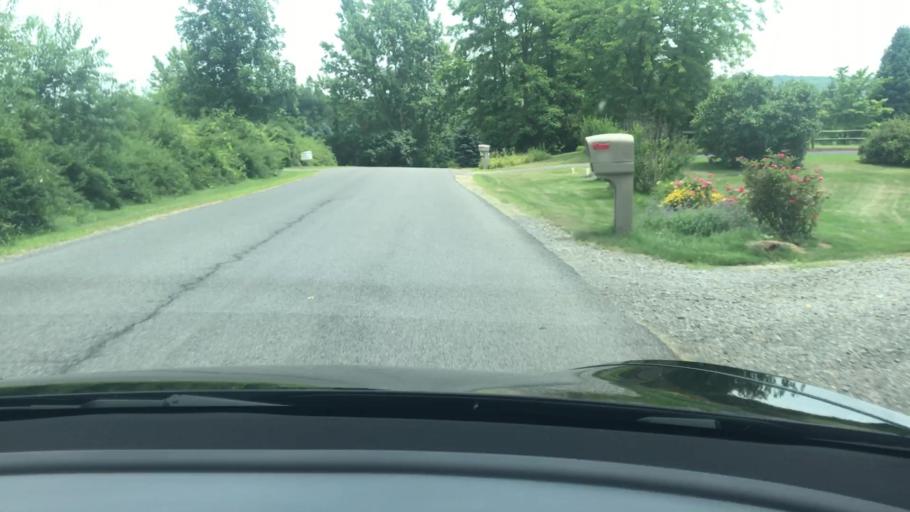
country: US
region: Pennsylvania
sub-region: Centre County
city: Stormstown
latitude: 40.7869
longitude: -78.0182
